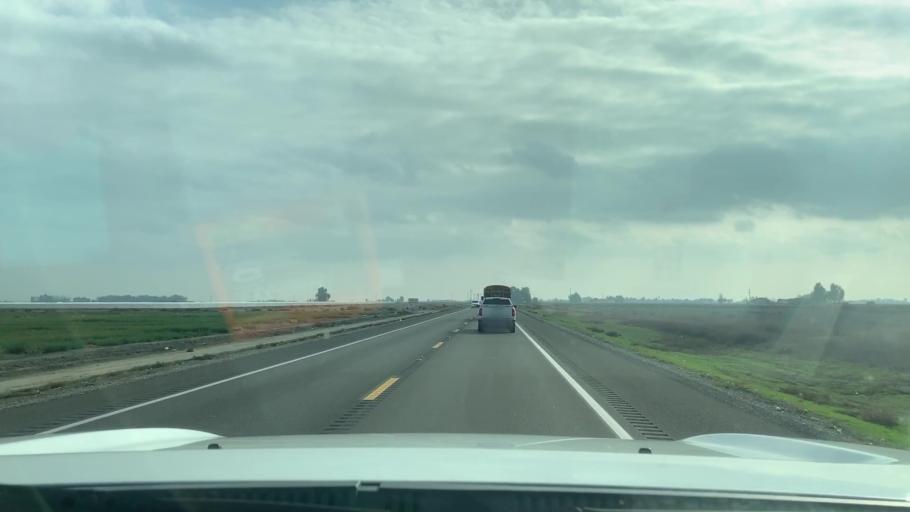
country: US
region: California
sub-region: Kings County
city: Stratford
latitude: 36.2205
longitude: -119.8162
